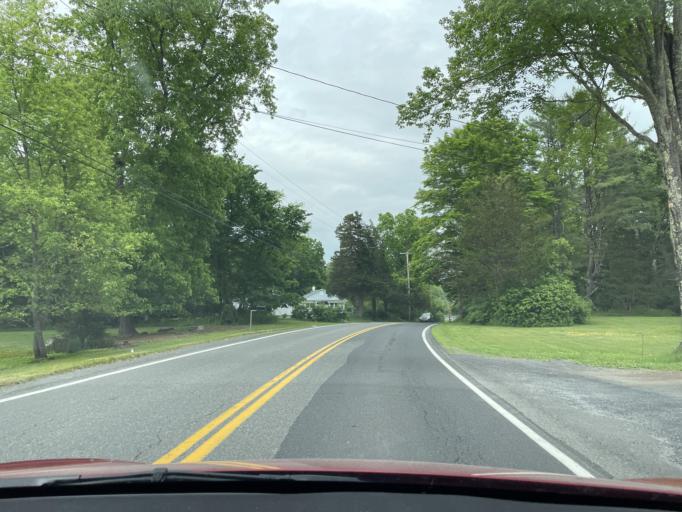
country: US
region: New York
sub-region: Ulster County
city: Zena
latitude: 42.0084
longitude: -74.0781
